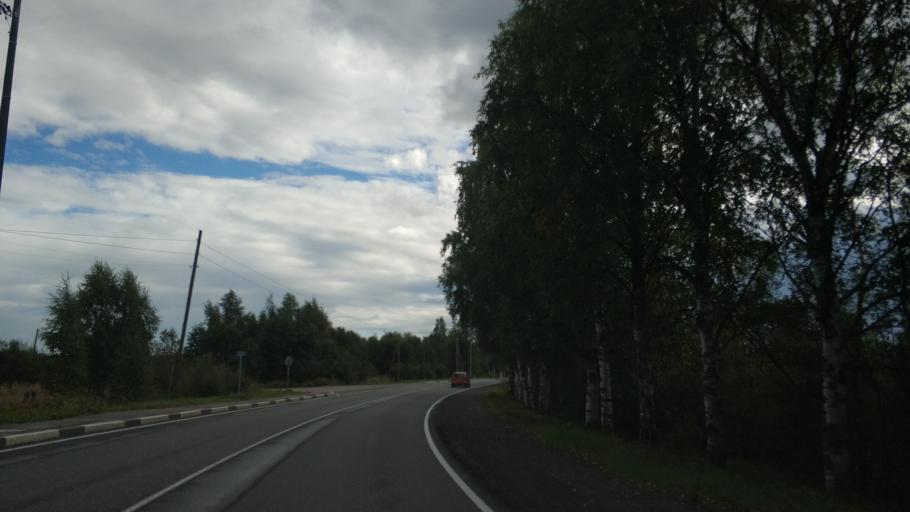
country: RU
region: Republic of Karelia
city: Khelyulya
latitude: 61.7444
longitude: 30.6796
